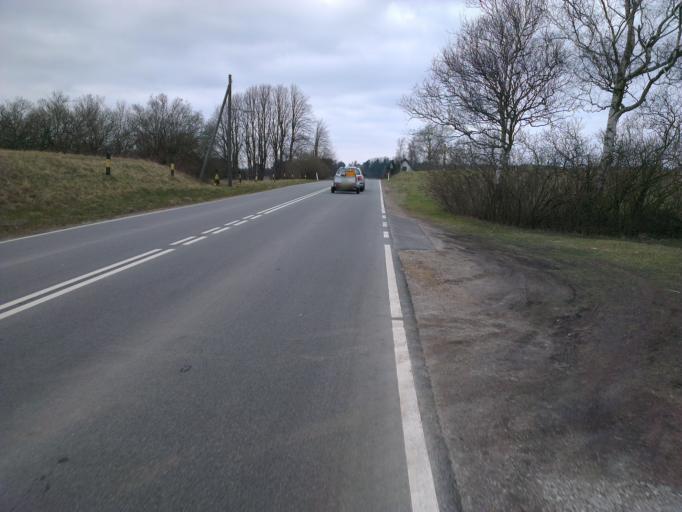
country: DK
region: Capital Region
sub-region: Frederikssund Kommune
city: Jaegerspris
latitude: 55.8876
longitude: 11.9554
